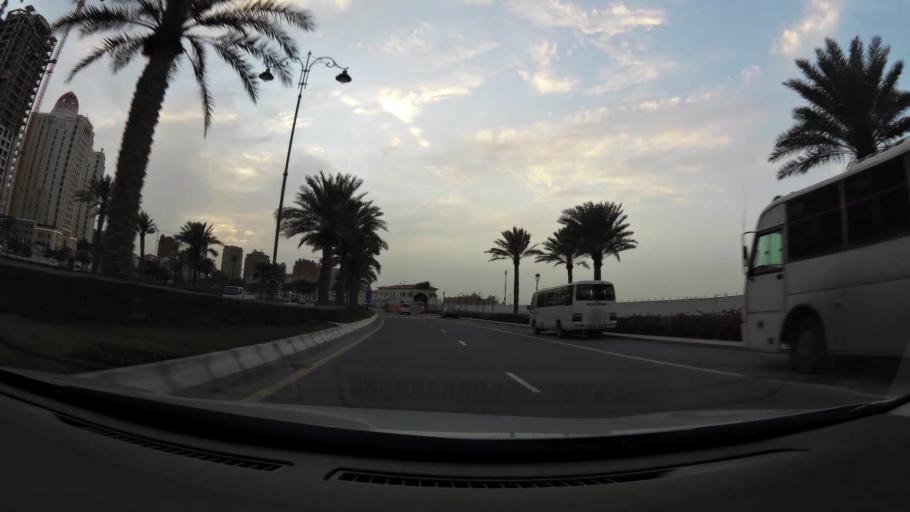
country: QA
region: Baladiyat ad Dawhah
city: Doha
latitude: 25.3717
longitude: 51.5589
